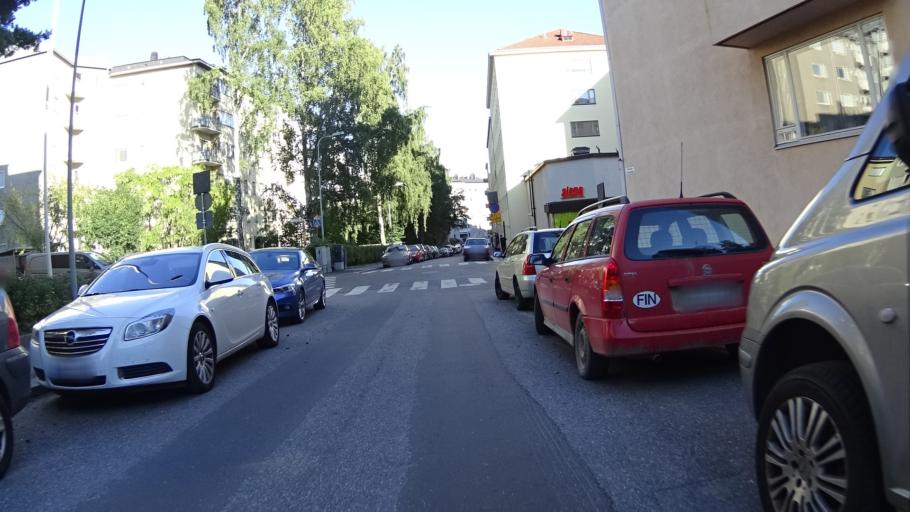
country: FI
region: Uusimaa
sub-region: Helsinki
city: Teekkarikylae
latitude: 60.1987
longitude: 24.8793
